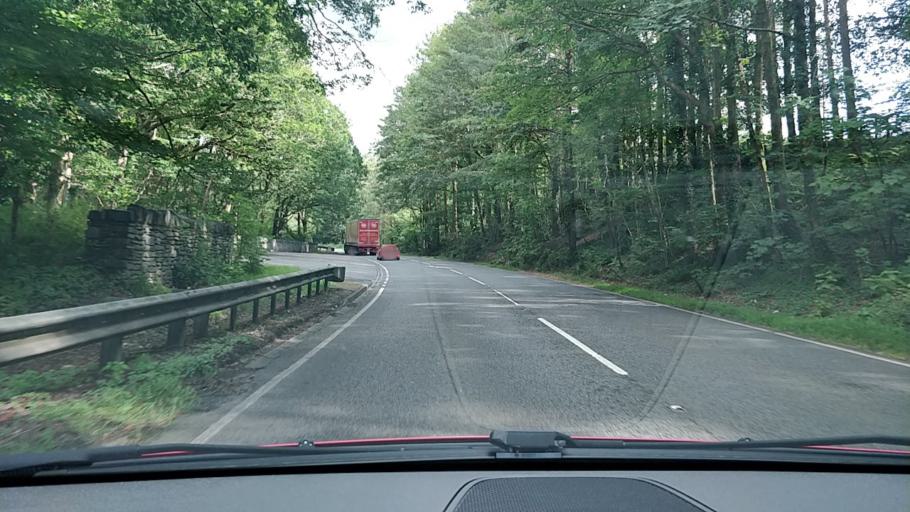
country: GB
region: Wales
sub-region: Gwynedd
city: Maentwrog
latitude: 52.9479
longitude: -3.9657
